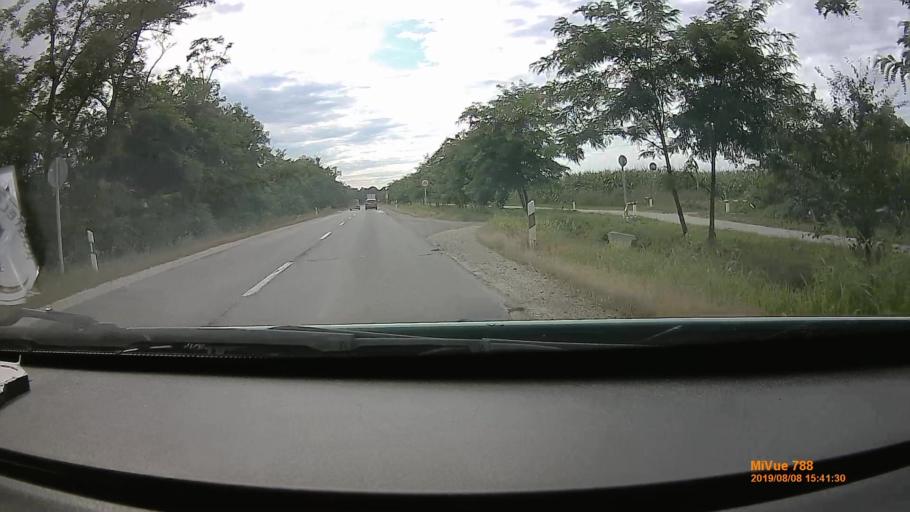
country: HU
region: Szabolcs-Szatmar-Bereg
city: Kocsord
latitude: 47.9380
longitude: 22.4108
